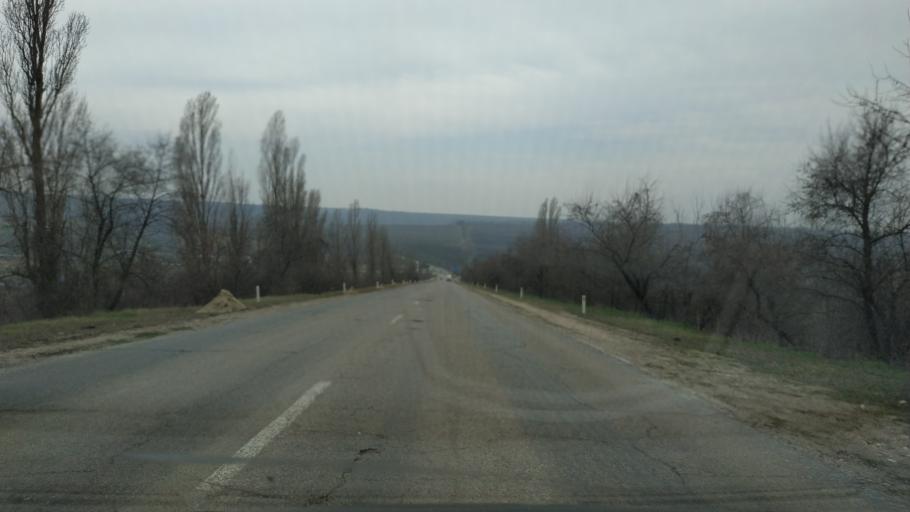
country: MD
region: Cahul
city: Cahul
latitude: 45.9560
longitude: 28.3548
